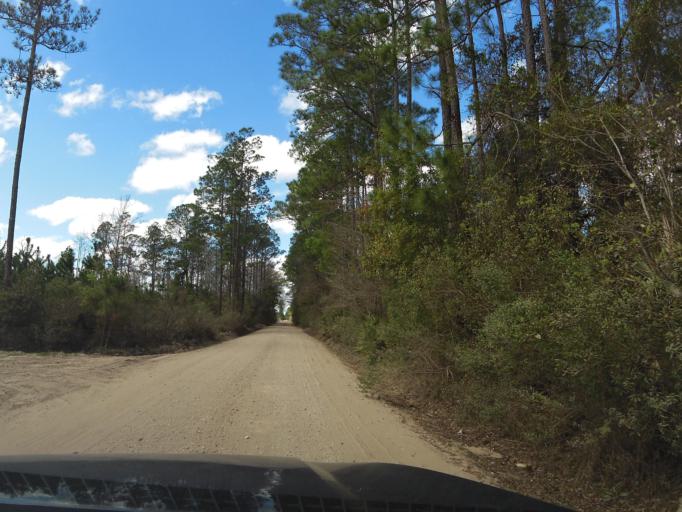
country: US
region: Florida
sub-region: Clay County
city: Green Cove Springs
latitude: 29.8366
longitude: -81.8044
